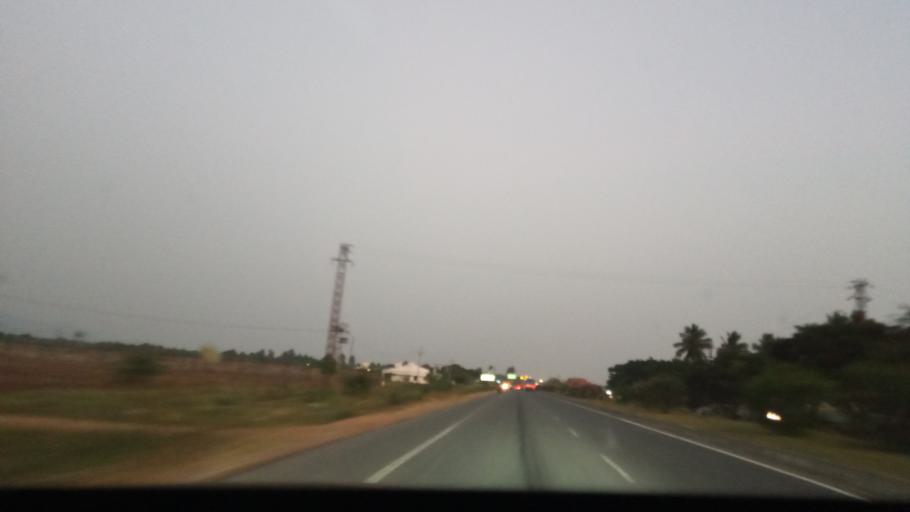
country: IN
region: Tamil Nadu
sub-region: Salem
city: Attur
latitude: 11.6184
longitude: 78.5551
